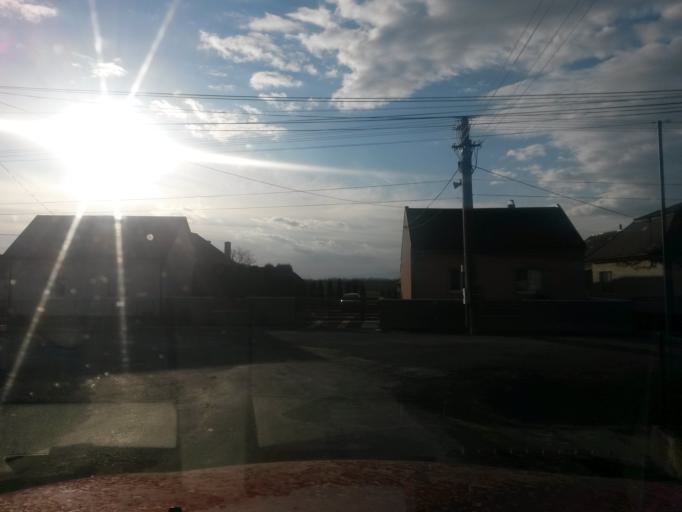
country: SK
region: Kosicky
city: Sobrance
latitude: 48.7389
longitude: 22.0795
